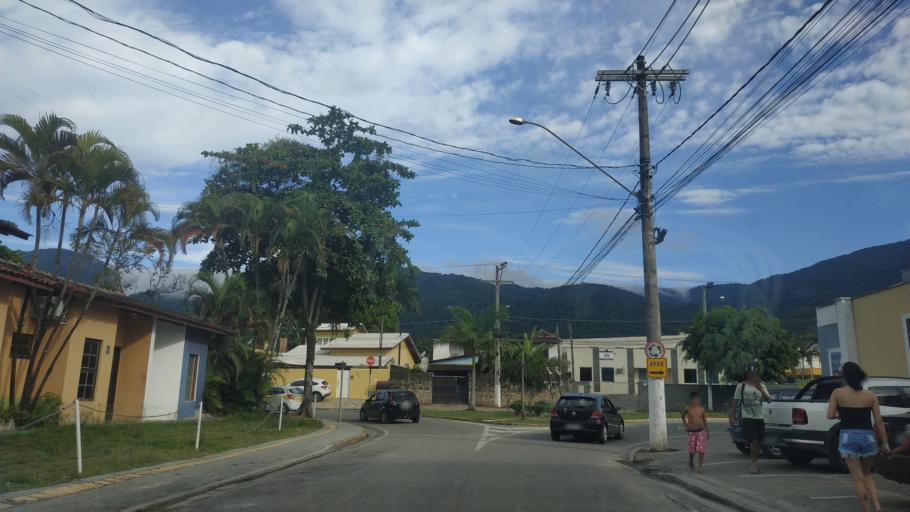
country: BR
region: Sao Paulo
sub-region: Ilhabela
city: Ilhabela
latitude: -23.8233
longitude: -45.3669
